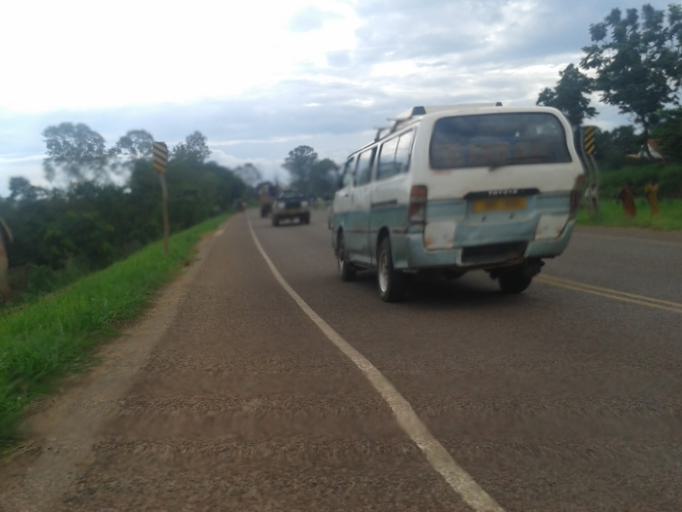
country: UG
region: Northern Region
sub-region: Gulu District
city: Gulu
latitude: 2.7622
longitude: 32.2747
